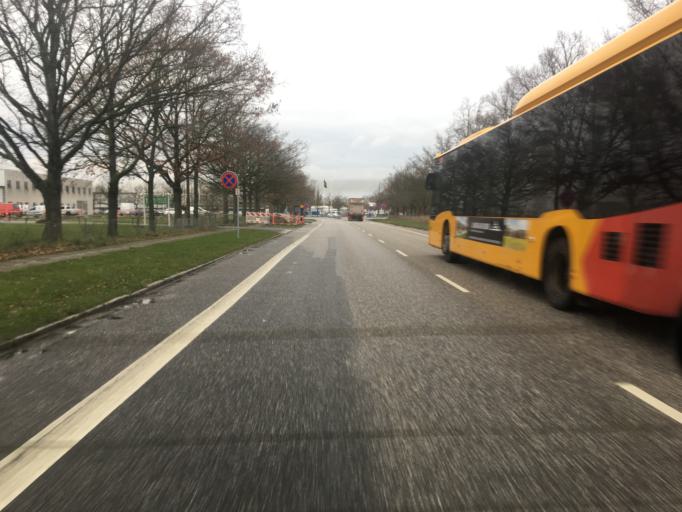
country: DK
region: Capital Region
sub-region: Hvidovre Kommune
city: Hvidovre
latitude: 55.6118
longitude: 12.4903
